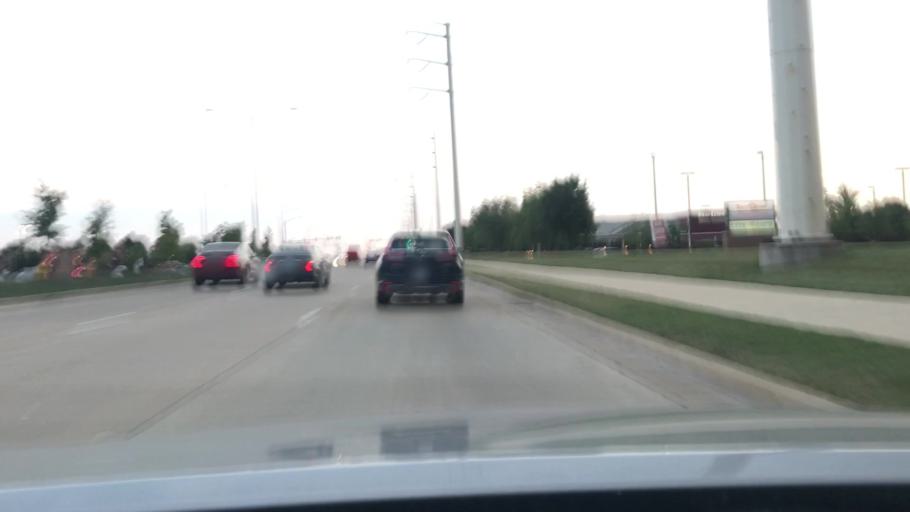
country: US
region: Illinois
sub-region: DuPage County
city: Warrenville
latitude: 41.7753
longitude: -88.2059
